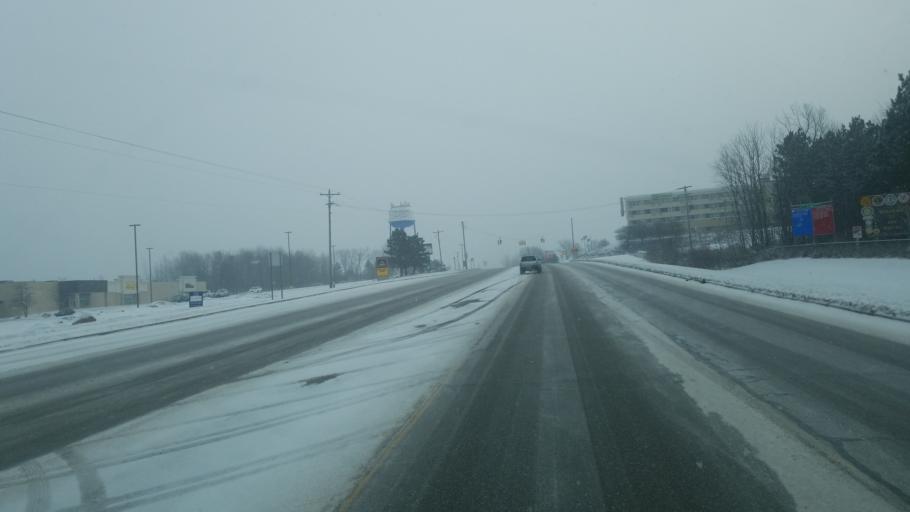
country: US
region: Michigan
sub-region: Mecosta County
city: Big Rapids
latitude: 43.6878
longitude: -85.5025
